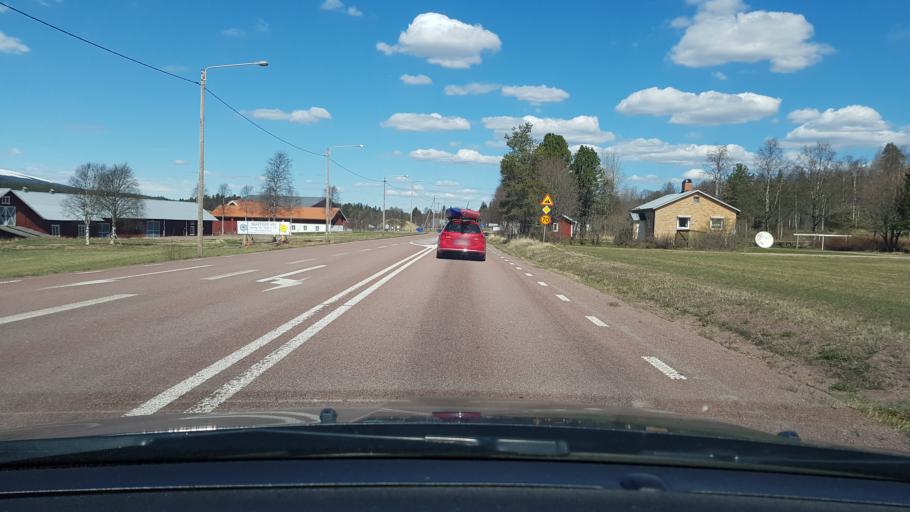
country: SE
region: Dalarna
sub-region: Malung-Saelens kommun
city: Malung
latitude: 61.0672
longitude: 13.3311
